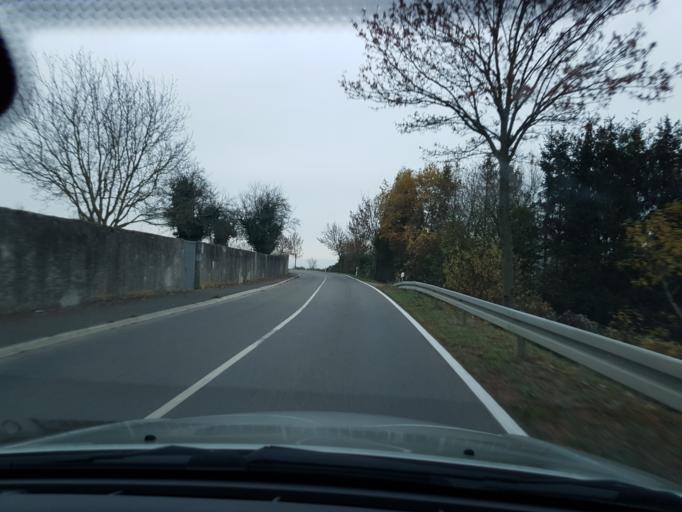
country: DE
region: Hesse
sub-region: Regierungsbezirk Darmstadt
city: Kiedrich
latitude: 50.0373
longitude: 8.0566
